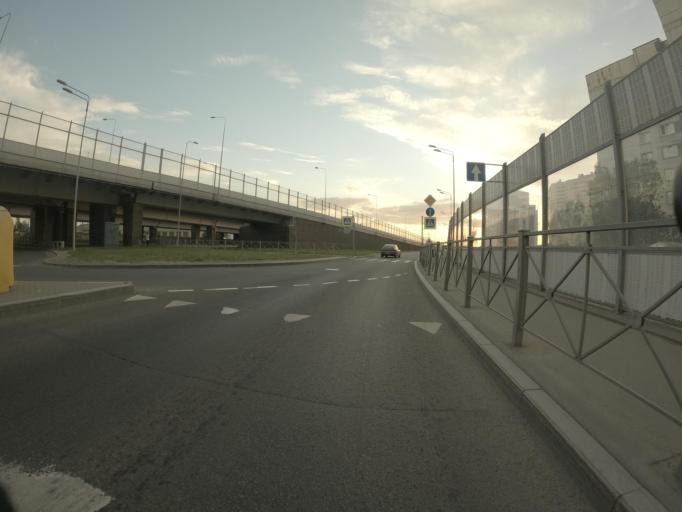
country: RU
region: St.-Petersburg
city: Kupchino
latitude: 59.8312
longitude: 30.3158
